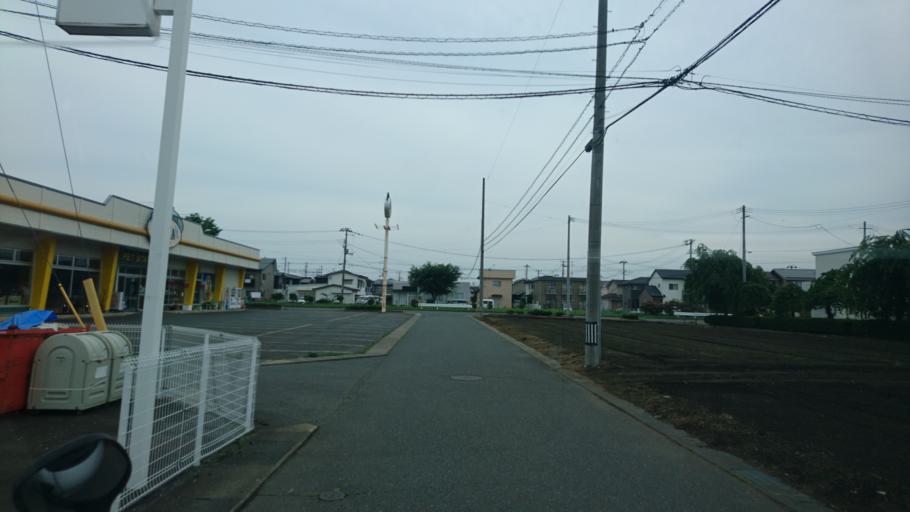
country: JP
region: Iwate
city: Morioka-shi
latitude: 39.6662
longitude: 141.1490
